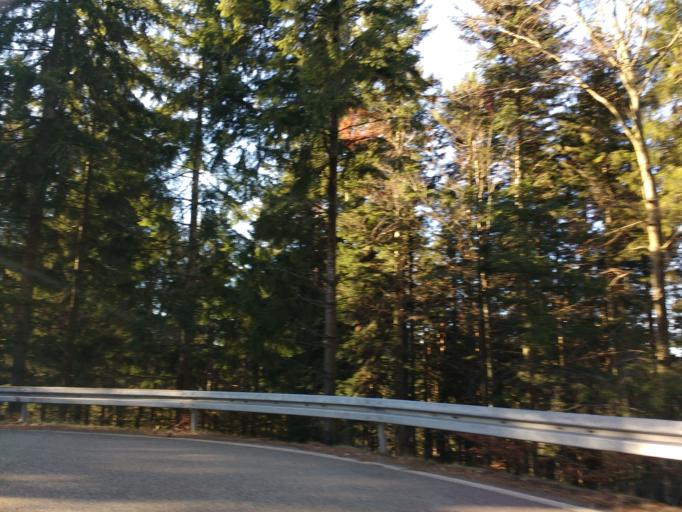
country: DE
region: Baden-Wuerttemberg
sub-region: Freiburg Region
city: Bad Peterstal-Griesbach
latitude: 48.4541
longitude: 8.2558
